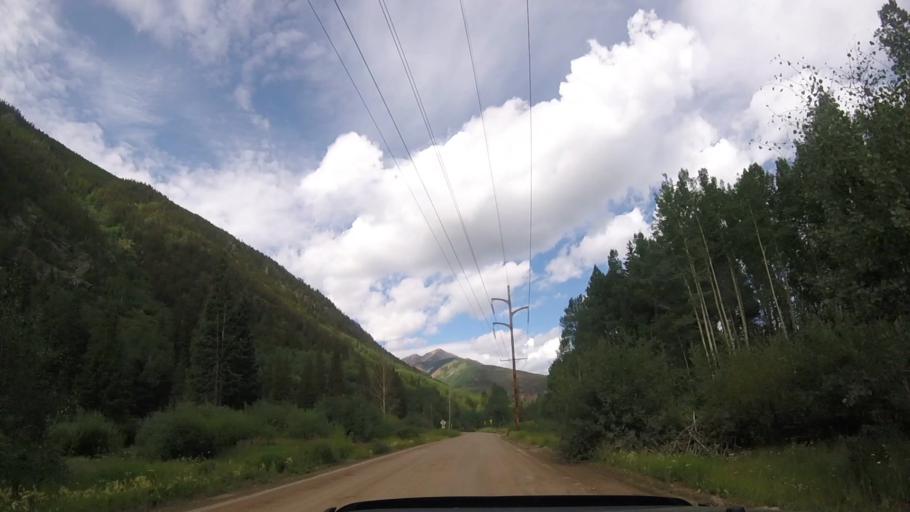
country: US
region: Colorado
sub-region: San Miguel County
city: Mountain Village
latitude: 37.8590
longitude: -107.8659
